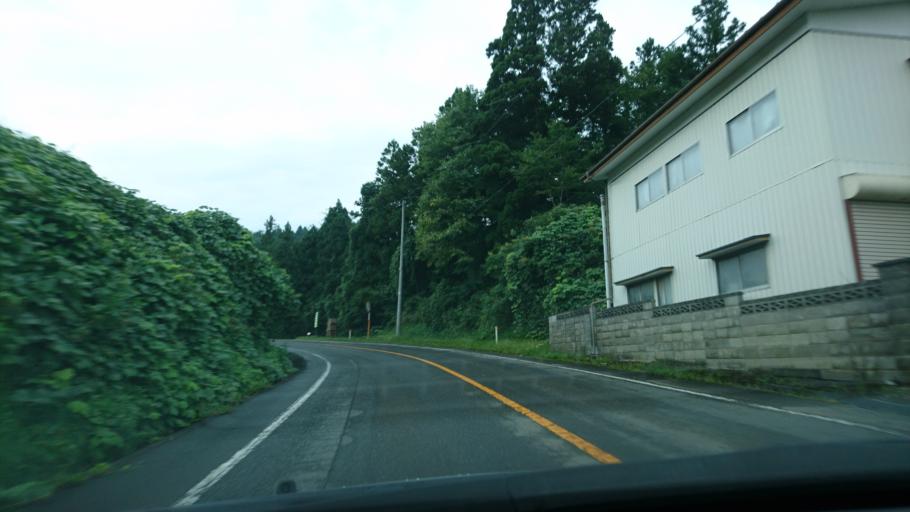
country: JP
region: Iwate
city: Ichinoseki
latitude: 39.0182
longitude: 141.2331
